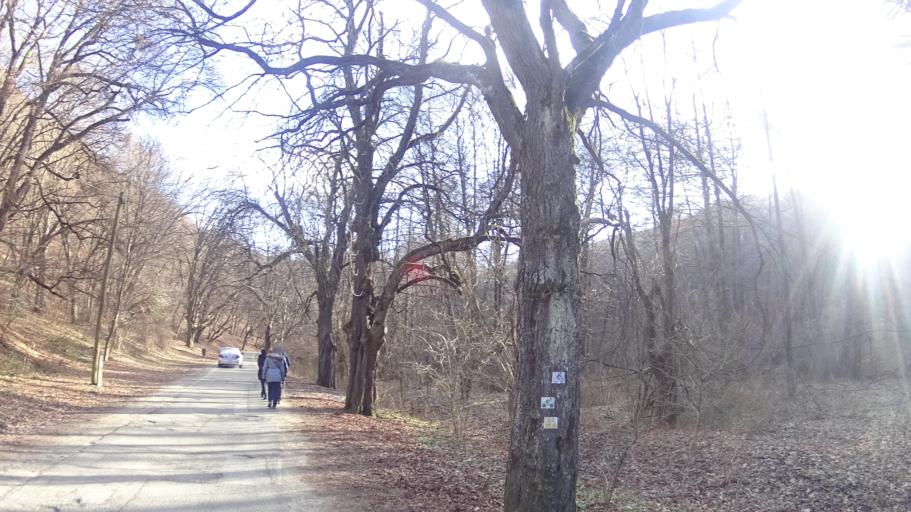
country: HU
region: Heves
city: Szilvasvarad
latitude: 48.0917
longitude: 20.3985
